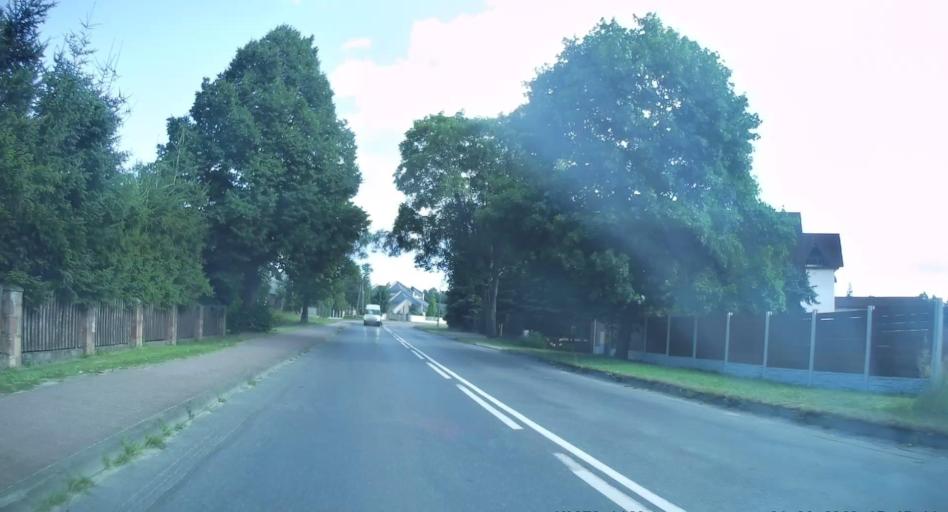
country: PL
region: Swietokrzyskie
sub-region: Powiat skarzyski
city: Suchedniow
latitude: 51.0327
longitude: 20.8392
